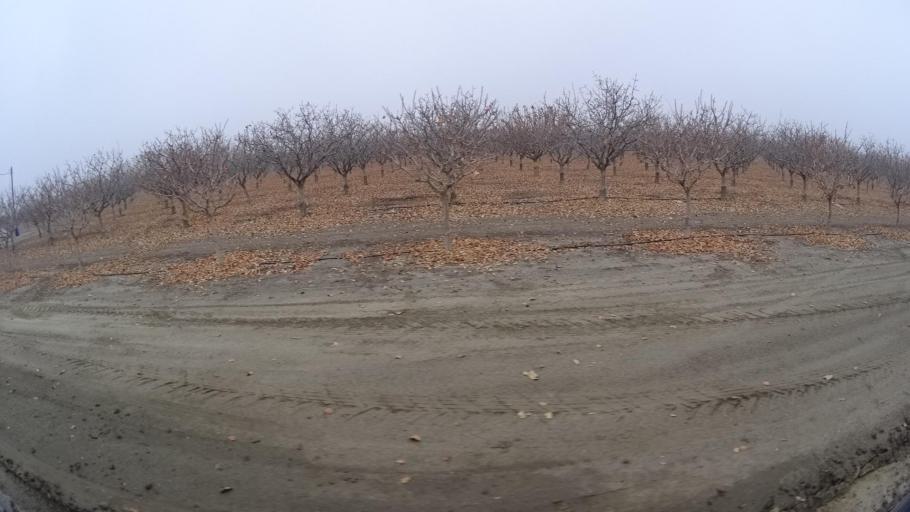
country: US
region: California
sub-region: Kern County
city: Buttonwillow
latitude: 35.4124
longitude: -119.5353
